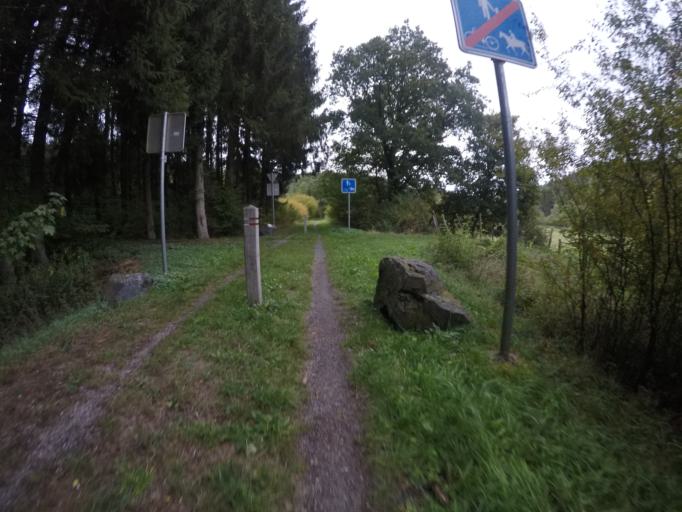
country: BE
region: Wallonia
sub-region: Province du Luxembourg
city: Fauvillers
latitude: 49.8623
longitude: 5.6939
